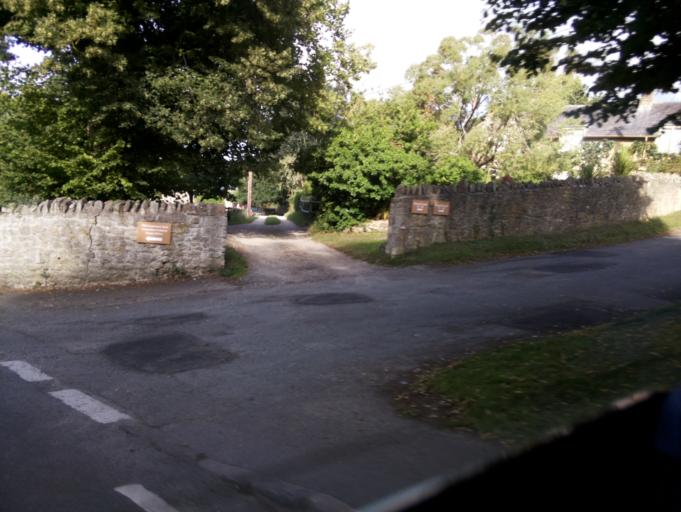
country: GB
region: England
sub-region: Oxfordshire
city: Shrivenham
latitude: 51.6418
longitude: -1.6607
